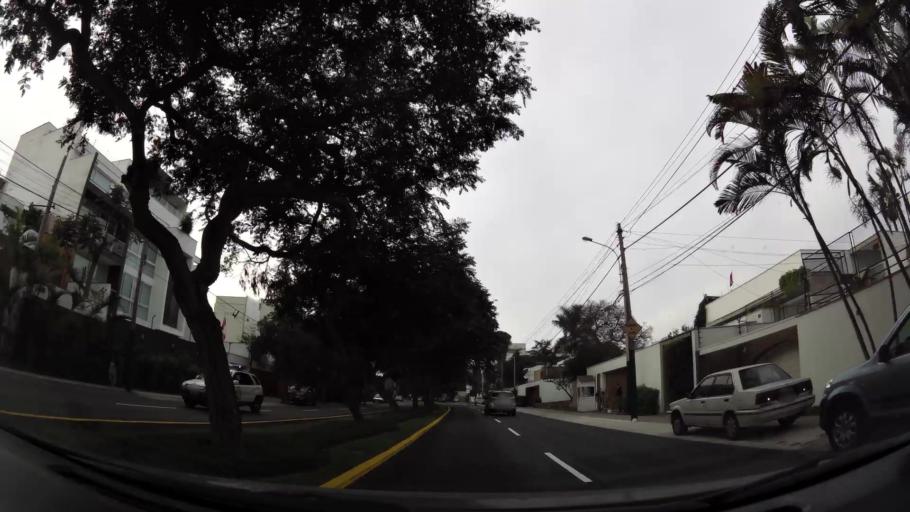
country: PE
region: Lima
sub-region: Lima
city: San Isidro
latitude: -12.1056
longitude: -77.0521
